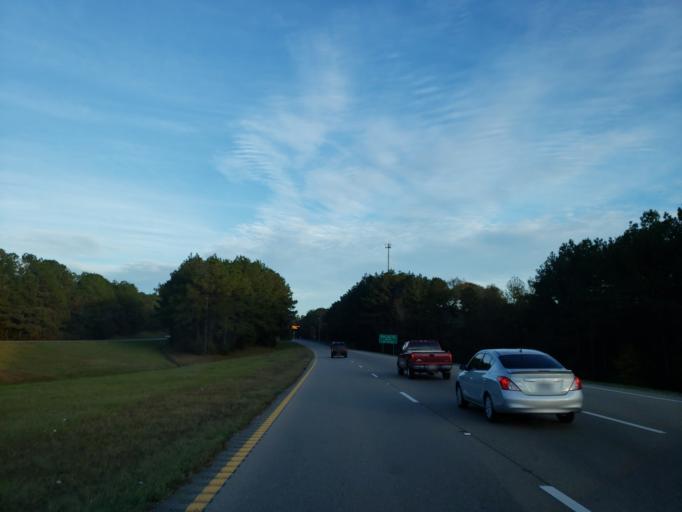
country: US
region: Mississippi
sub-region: Forrest County
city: Hattiesburg
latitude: 31.2381
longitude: -89.3156
